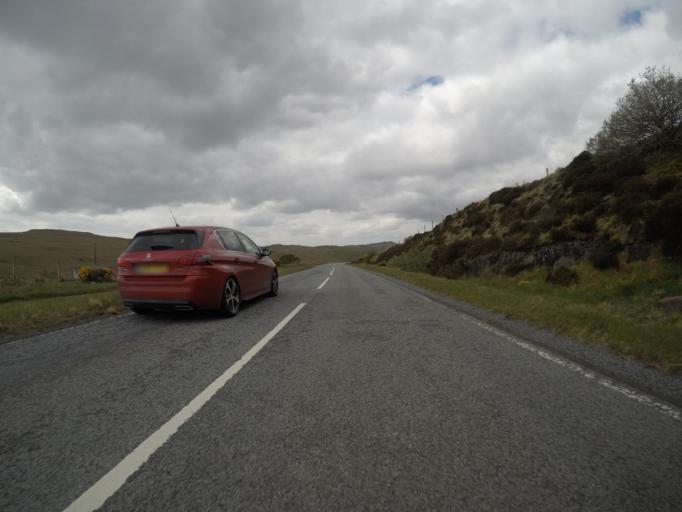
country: GB
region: Scotland
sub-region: Highland
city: Isle of Skye
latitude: 57.3208
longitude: -6.3258
